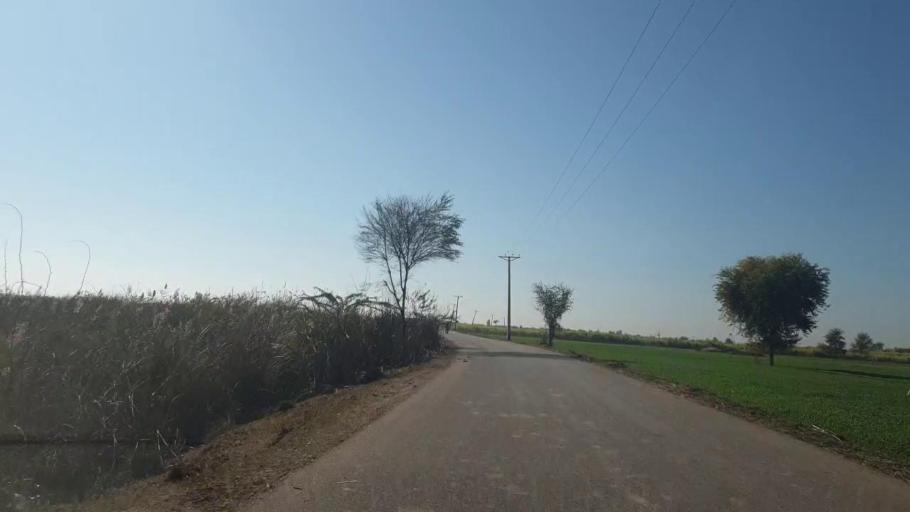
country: PK
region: Sindh
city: Kot Diji
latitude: 27.3079
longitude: 68.6465
